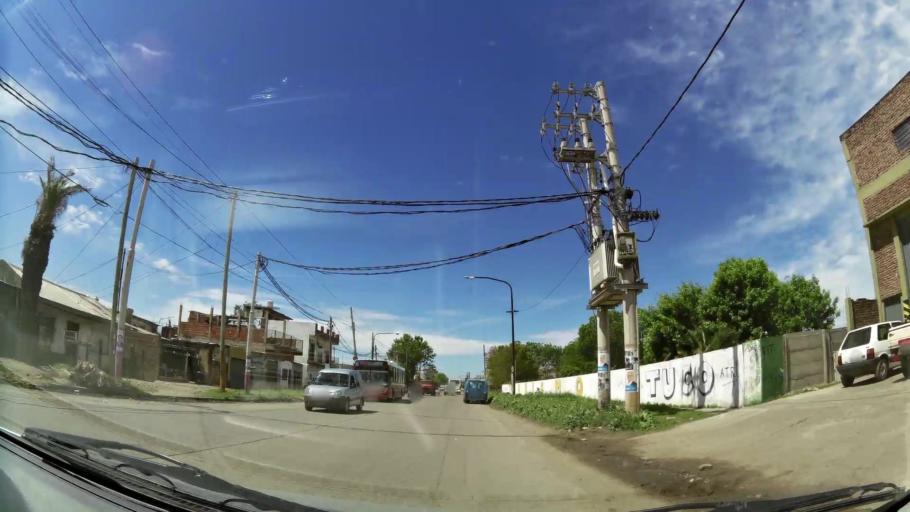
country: AR
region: Buenos Aires
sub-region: Partido de Quilmes
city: Quilmes
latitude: -34.7499
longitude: -58.3040
